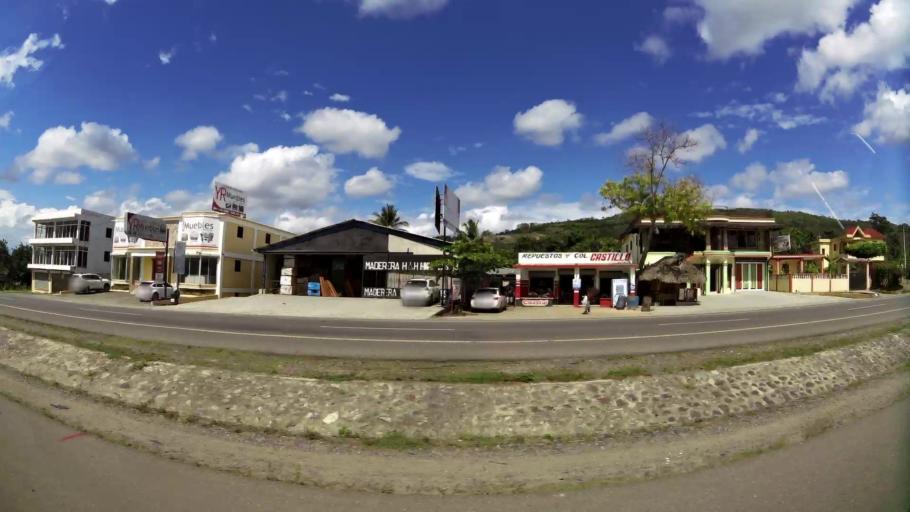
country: DO
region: La Vega
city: Rio Verde Arriba
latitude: 19.2991
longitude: -70.5813
